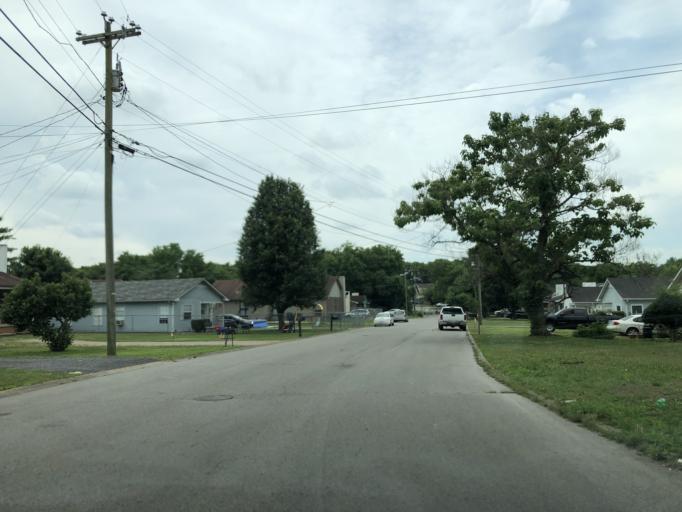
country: US
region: Tennessee
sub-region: Davidson County
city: Nashville
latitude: 36.2456
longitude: -86.7755
